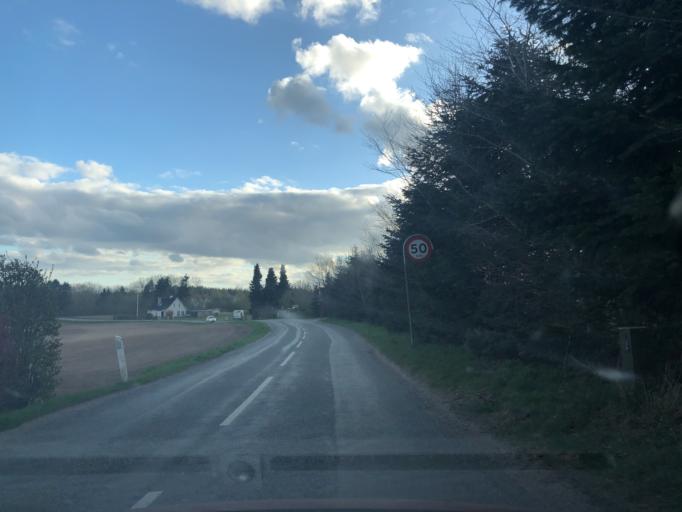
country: DK
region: Zealand
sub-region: Lejre Kommune
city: Kirke Hvalso
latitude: 55.5014
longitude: 11.8608
